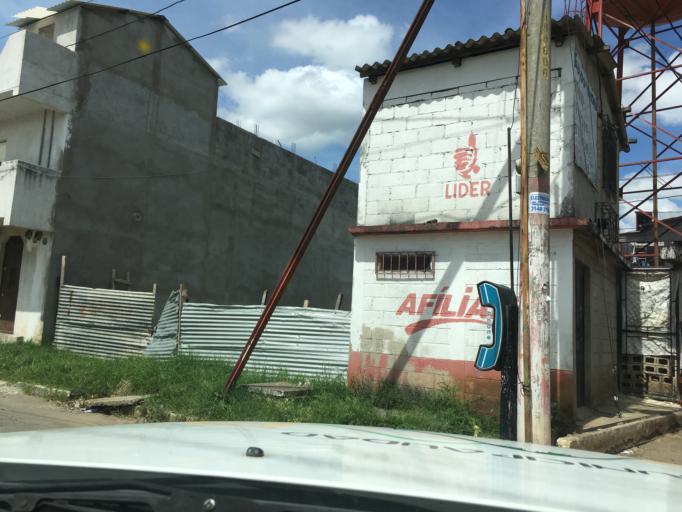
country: GT
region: Guatemala
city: Petapa
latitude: 14.5037
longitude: -90.5674
